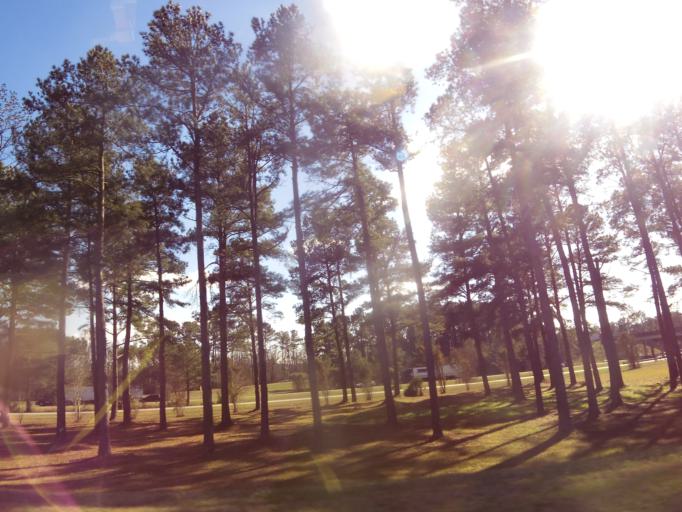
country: US
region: South Carolina
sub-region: Clarendon County
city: Manning
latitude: 33.5907
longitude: -80.3558
